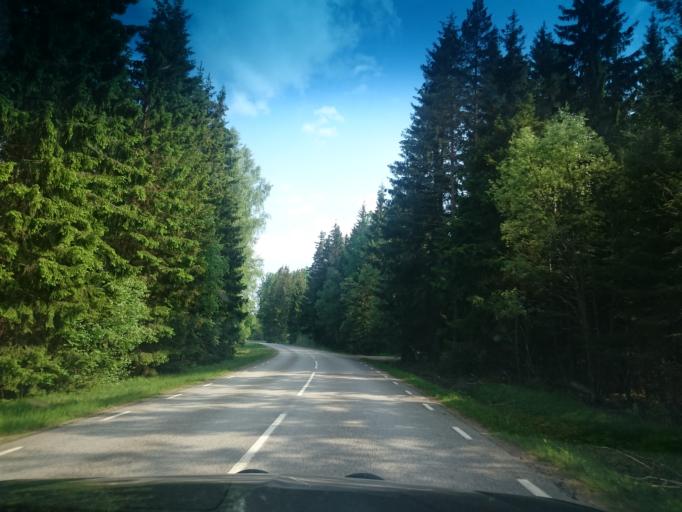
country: SE
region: Joenkoeping
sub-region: Vetlanda Kommun
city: Vetlanda
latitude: 57.3695
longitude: 15.0540
